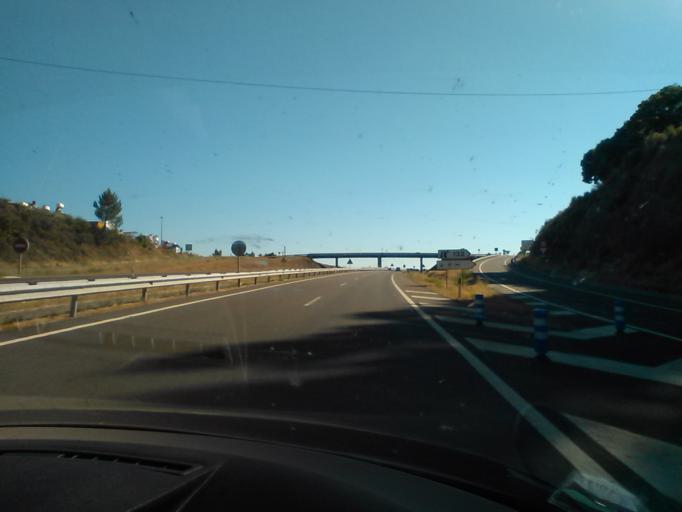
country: ES
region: Galicia
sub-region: Provincia de Ourense
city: Rios
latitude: 42.0275
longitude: -7.1815
